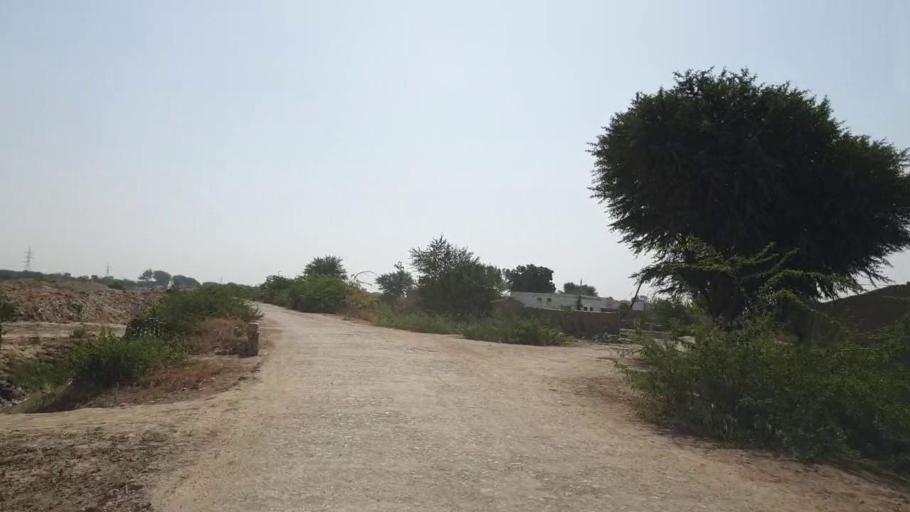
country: PK
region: Sindh
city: Naukot
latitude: 25.0015
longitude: 69.4663
